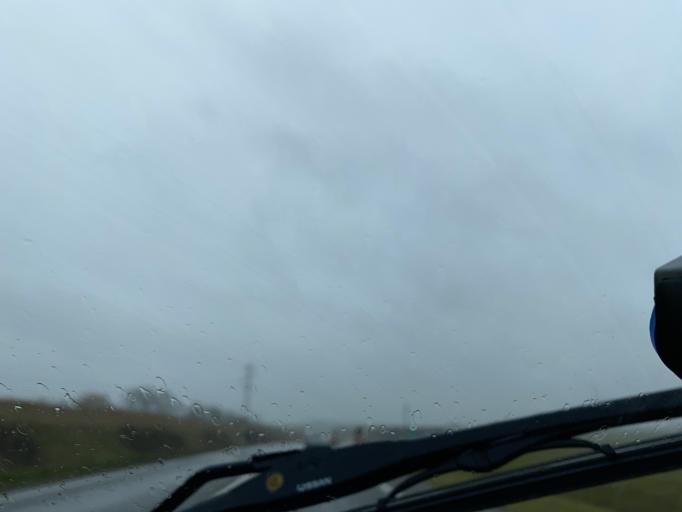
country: FR
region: Centre
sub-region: Departement d'Eure-et-Loir
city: Leves
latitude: 48.4716
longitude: 1.4639
